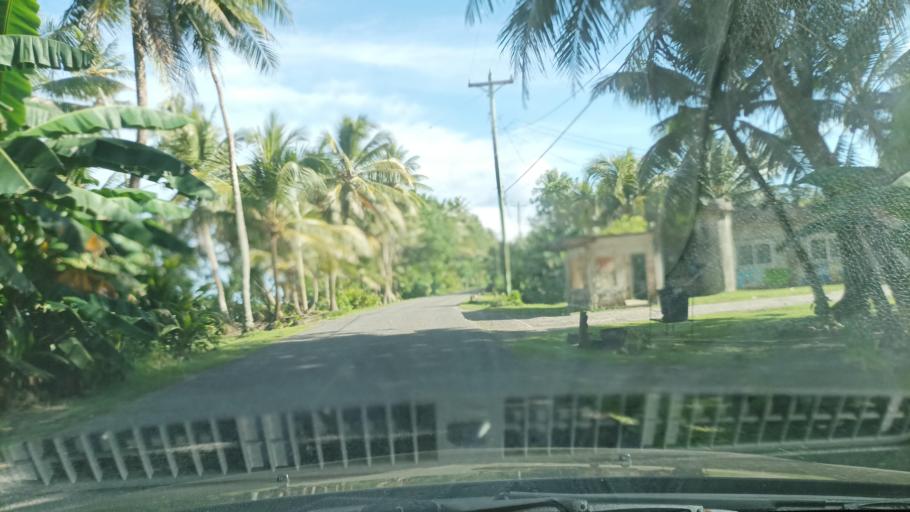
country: FM
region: Kosrae
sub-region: Malem Municipality
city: Malem
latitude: 5.2991
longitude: 163.0301
